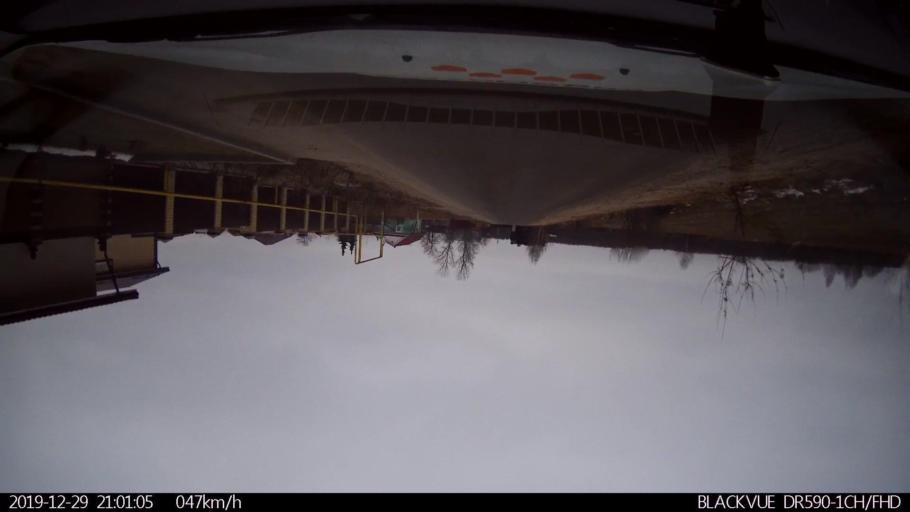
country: RU
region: Nizjnij Novgorod
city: Afonino
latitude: 56.1864
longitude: 43.9900
